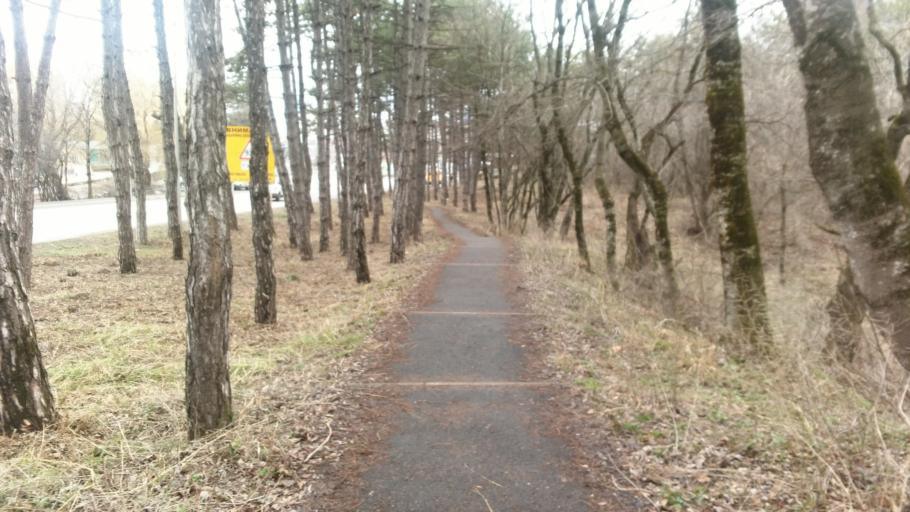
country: RU
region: Stavropol'skiy
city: Zheleznovodsk
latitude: 44.1393
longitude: 43.0138
